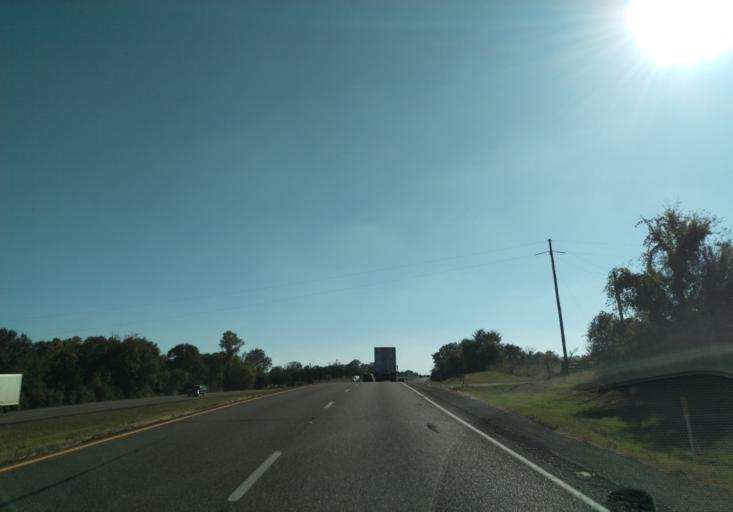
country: US
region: Texas
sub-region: Grimes County
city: Navasota
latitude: 30.2494
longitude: -96.0462
